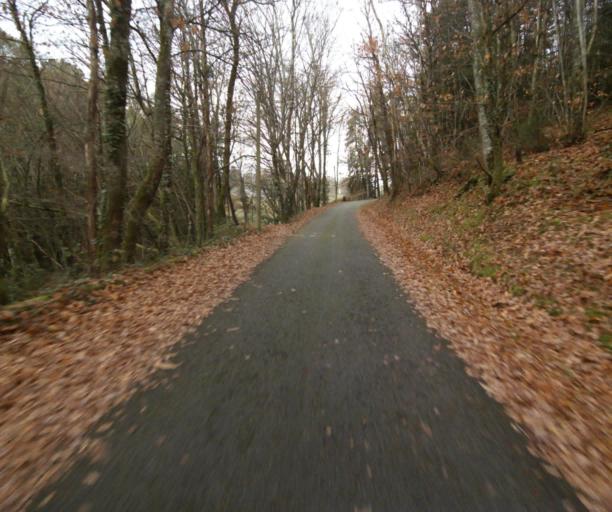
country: FR
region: Limousin
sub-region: Departement de la Correze
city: Chameyrat
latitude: 45.2260
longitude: 1.6969
